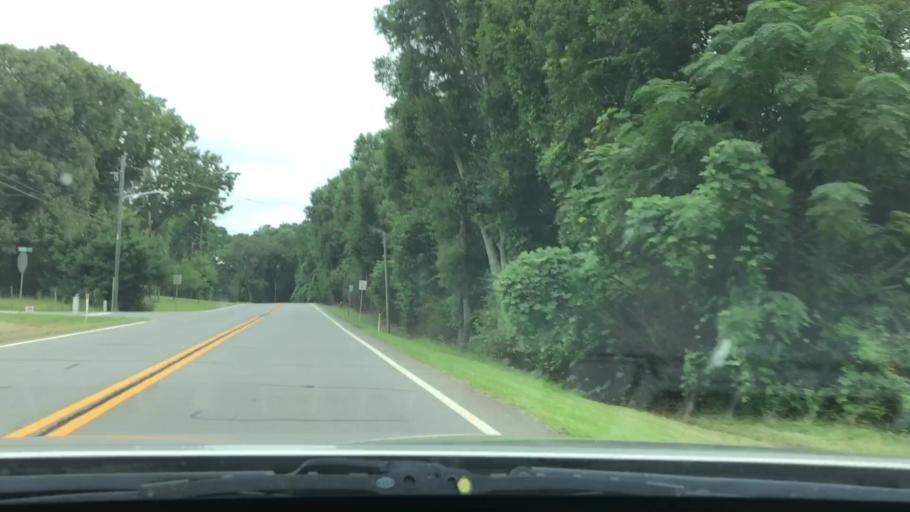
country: US
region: Georgia
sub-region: Upson County
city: Hannahs Mill
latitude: 33.0152
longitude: -84.4986
